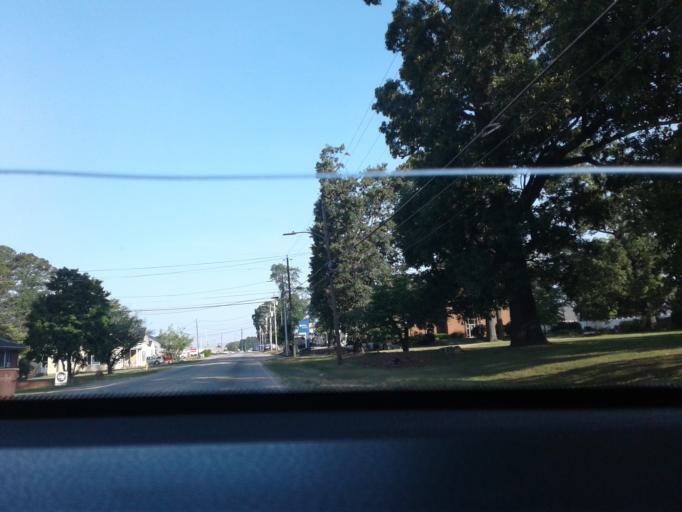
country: US
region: North Carolina
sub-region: Harnett County
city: Dunn
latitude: 35.3141
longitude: -78.6205
